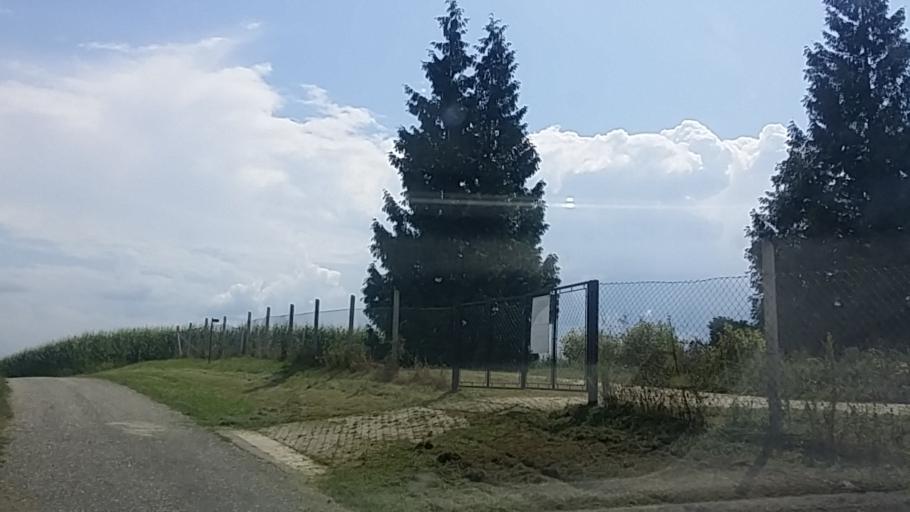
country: HR
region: Medimurska
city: Podturen
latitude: 46.5192
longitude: 16.5500
